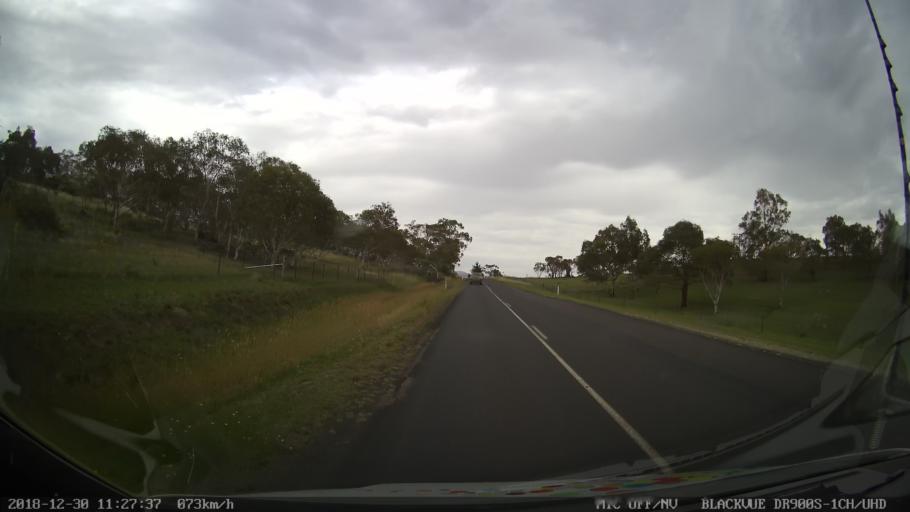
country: AU
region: New South Wales
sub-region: Snowy River
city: Jindabyne
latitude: -36.4590
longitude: 148.6254
